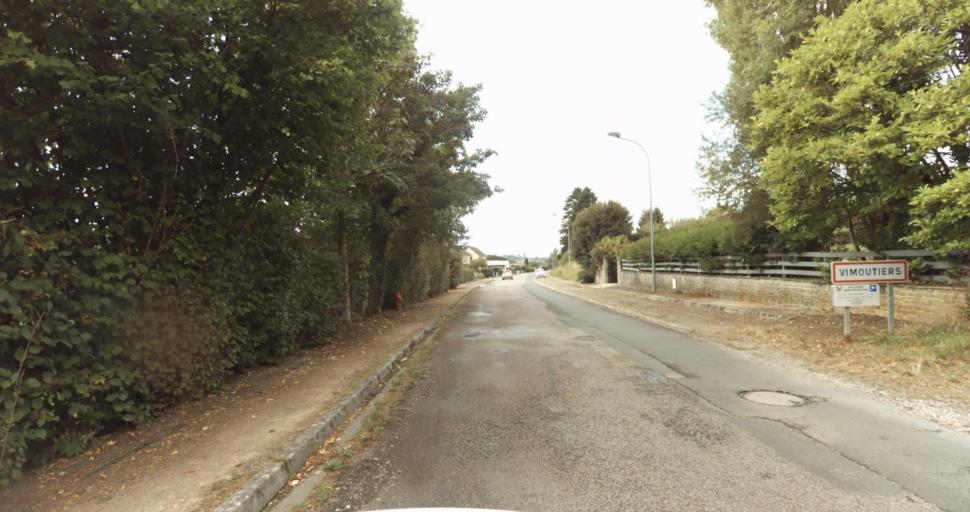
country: FR
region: Lower Normandy
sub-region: Departement de l'Orne
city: Vimoutiers
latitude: 48.9213
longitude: 0.2061
